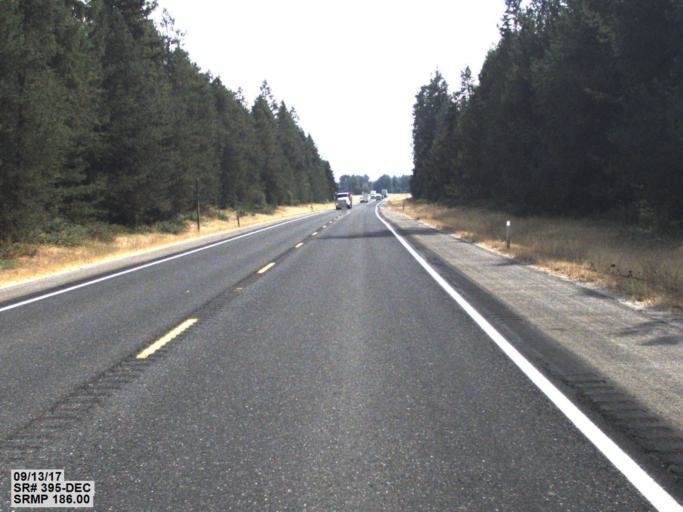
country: US
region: Washington
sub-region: Spokane County
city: Deer Park
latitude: 48.0023
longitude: -117.5759
